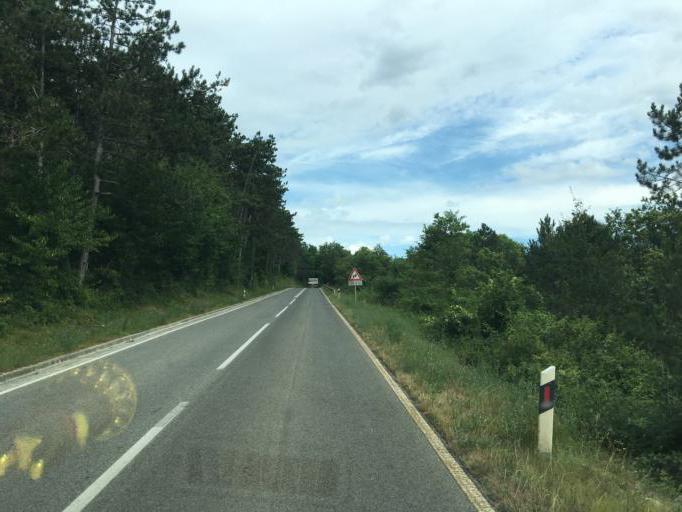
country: HR
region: Istarska
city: Karojba
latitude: 45.2682
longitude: 13.8632
